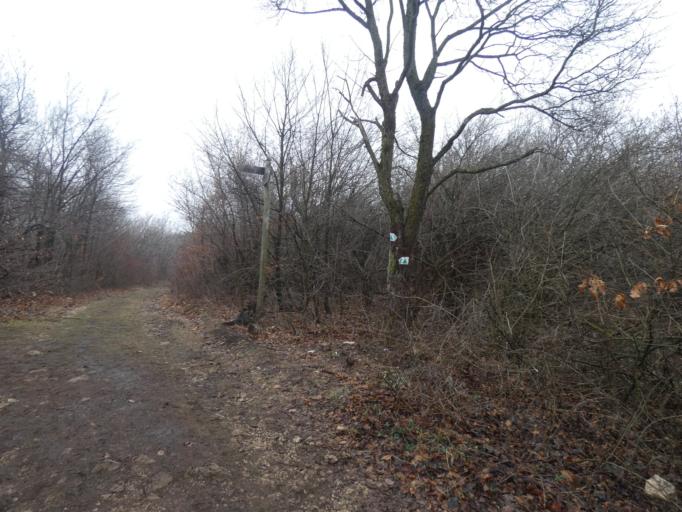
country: HU
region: Pest
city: Telki
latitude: 47.5508
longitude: 18.8664
